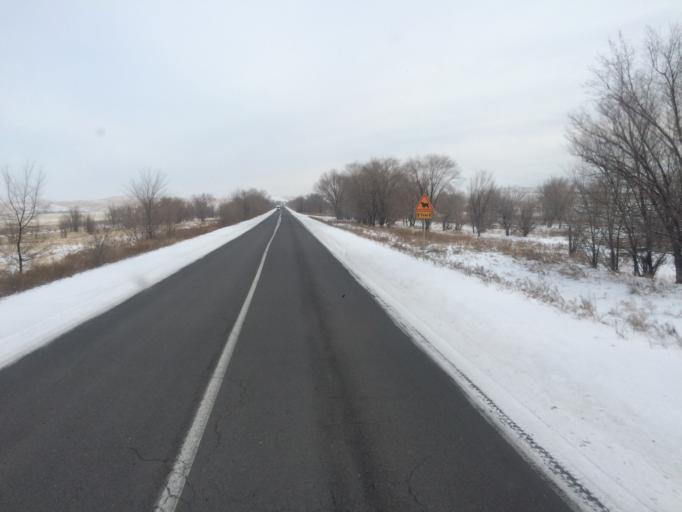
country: KG
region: Chuy
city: Bystrovka
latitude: 43.3278
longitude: 75.9007
